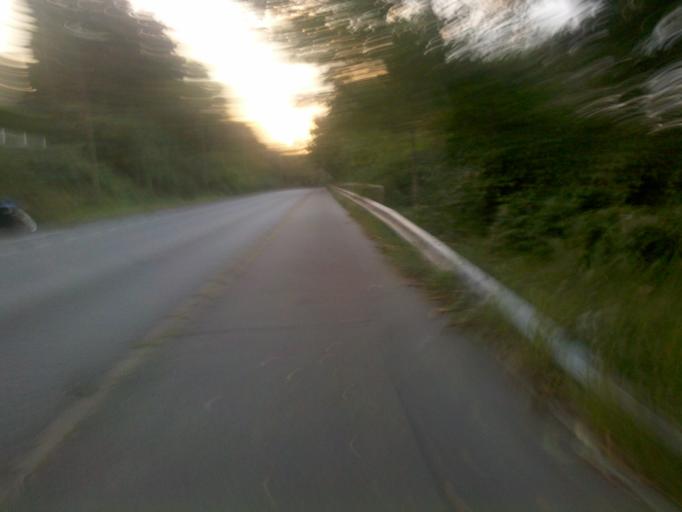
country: DE
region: Baden-Wuerttemberg
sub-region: Karlsruhe Region
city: Eppelheim
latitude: 49.4106
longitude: 8.6625
